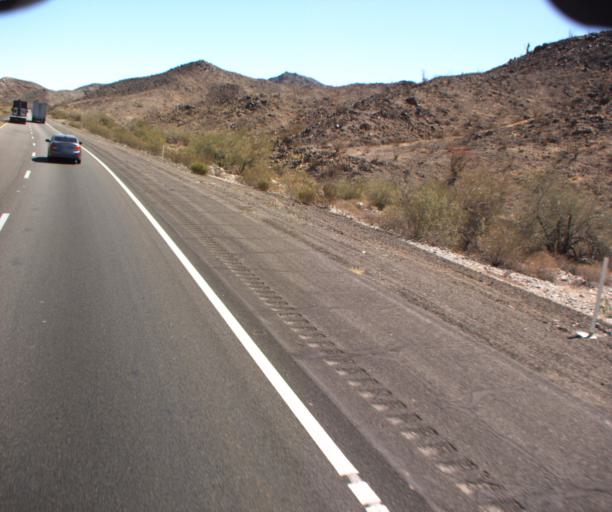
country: US
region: Arizona
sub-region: Yuma County
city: Fortuna Foothills
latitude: 32.6579
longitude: -114.3429
